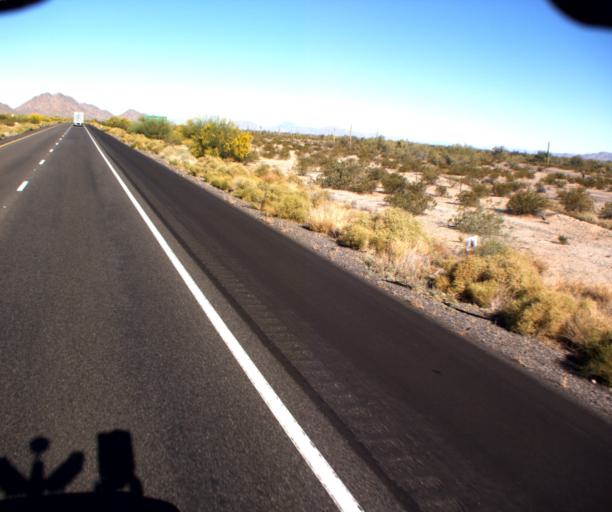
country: US
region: Arizona
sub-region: Maricopa County
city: Gila Bend
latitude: 32.8959
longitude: -112.4997
